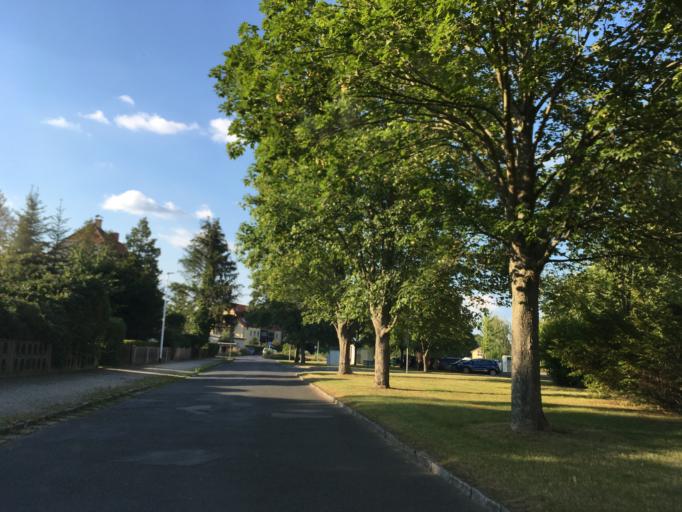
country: DE
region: Saxony
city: Radeberg
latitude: 51.1057
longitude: 13.9180
